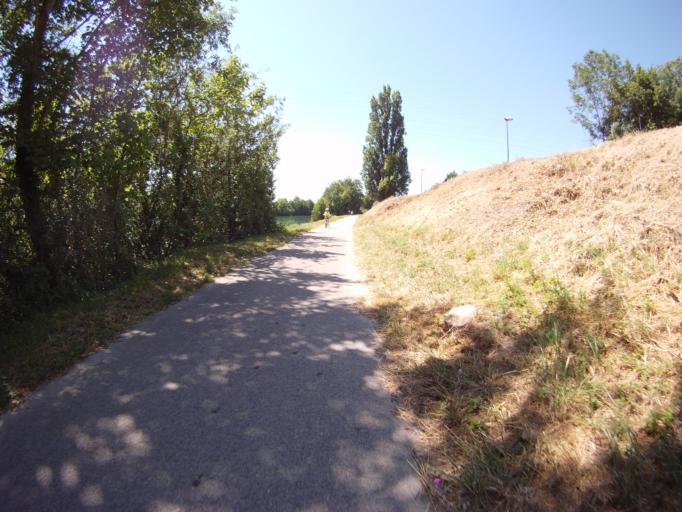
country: FR
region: Champagne-Ardenne
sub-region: Departement de la Marne
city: Damery
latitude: 49.0725
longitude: 3.8708
